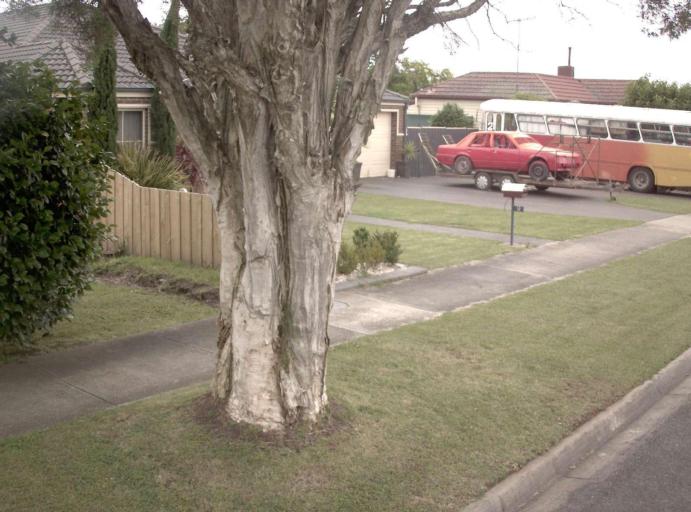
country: AU
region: Victoria
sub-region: Latrobe
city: Moe
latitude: -38.2096
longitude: 146.1518
